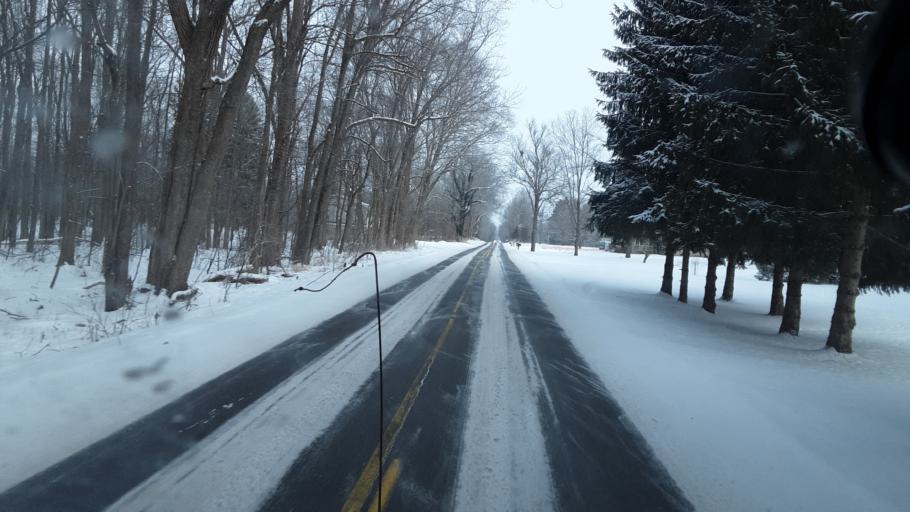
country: US
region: Michigan
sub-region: Jackson County
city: Jackson
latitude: 42.3131
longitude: -84.4829
